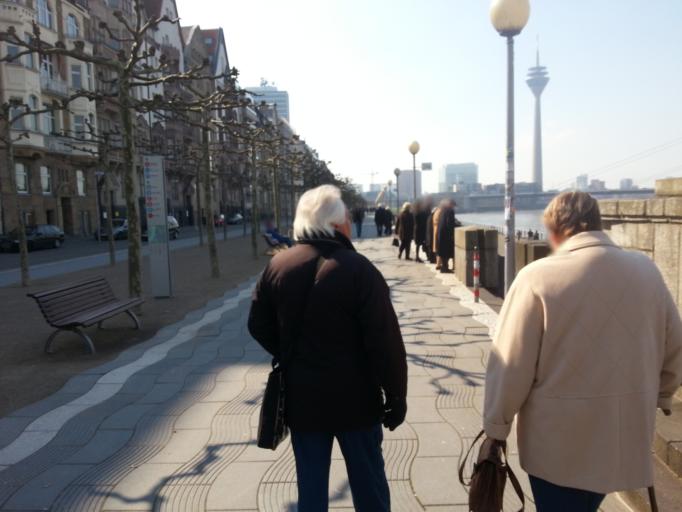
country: DE
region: North Rhine-Westphalia
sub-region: Regierungsbezirk Dusseldorf
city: Dusseldorf
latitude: 51.2244
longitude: 6.7693
